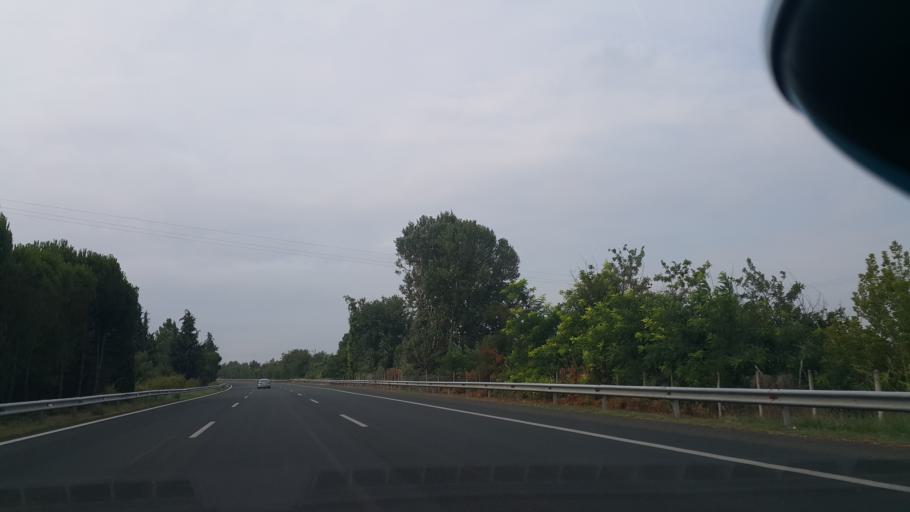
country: GR
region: Central Macedonia
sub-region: Nomos Pierias
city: Aiginio
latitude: 40.4993
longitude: 22.5653
